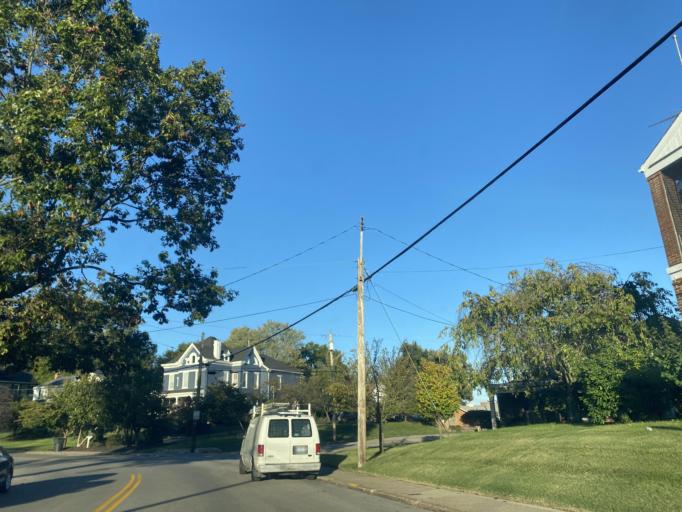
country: US
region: Kentucky
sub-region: Campbell County
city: Fort Thomas
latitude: 39.0963
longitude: -84.4503
